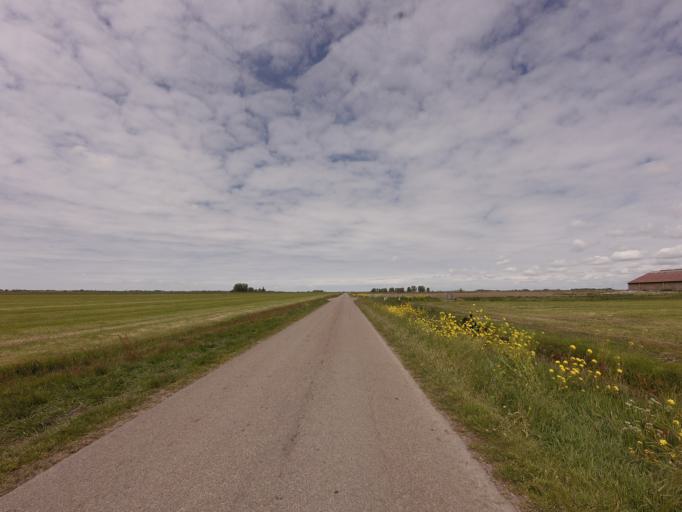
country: NL
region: Friesland
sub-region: Gemeente Gaasterlan-Sleat
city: Oudemirdum
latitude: 52.9024
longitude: 5.5068
